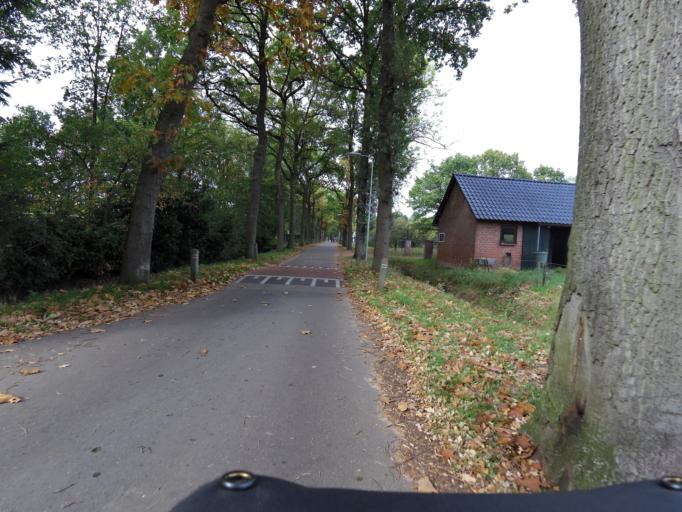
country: BE
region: Flanders
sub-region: Provincie Antwerpen
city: Stabroek
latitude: 51.3681
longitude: 4.4005
